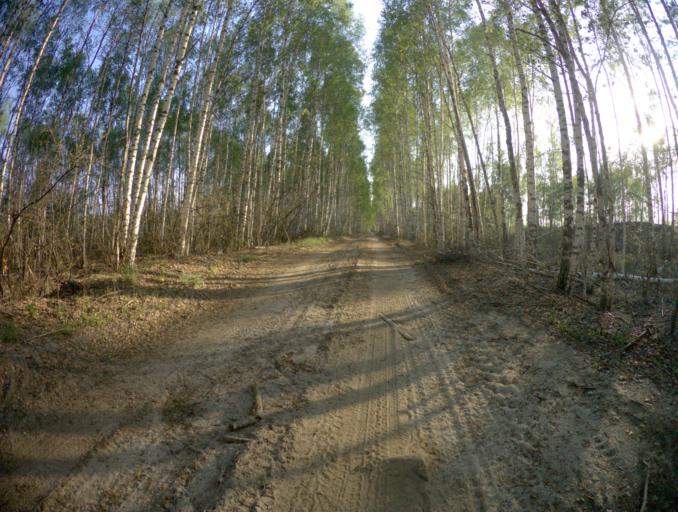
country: RU
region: Vladimir
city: Vyazniki
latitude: 56.3705
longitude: 42.1620
